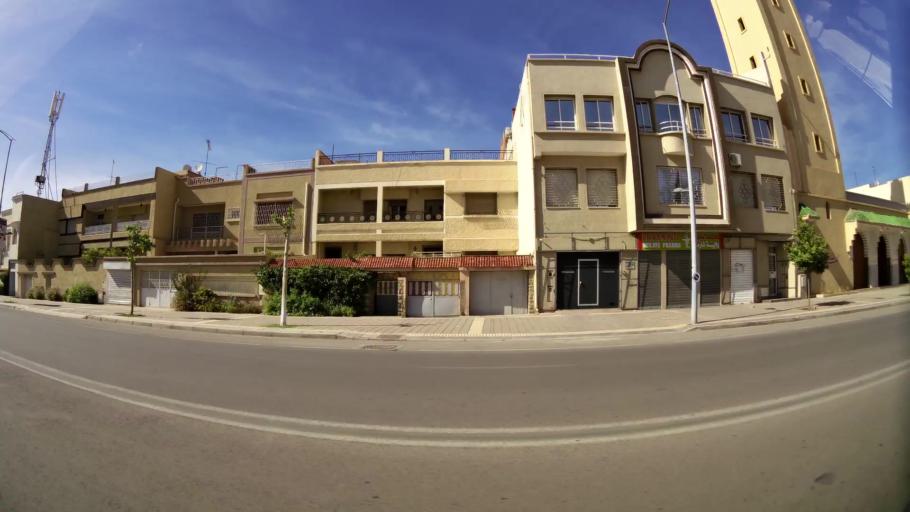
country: MA
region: Oriental
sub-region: Oujda-Angad
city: Oujda
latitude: 34.6653
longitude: -1.9128
